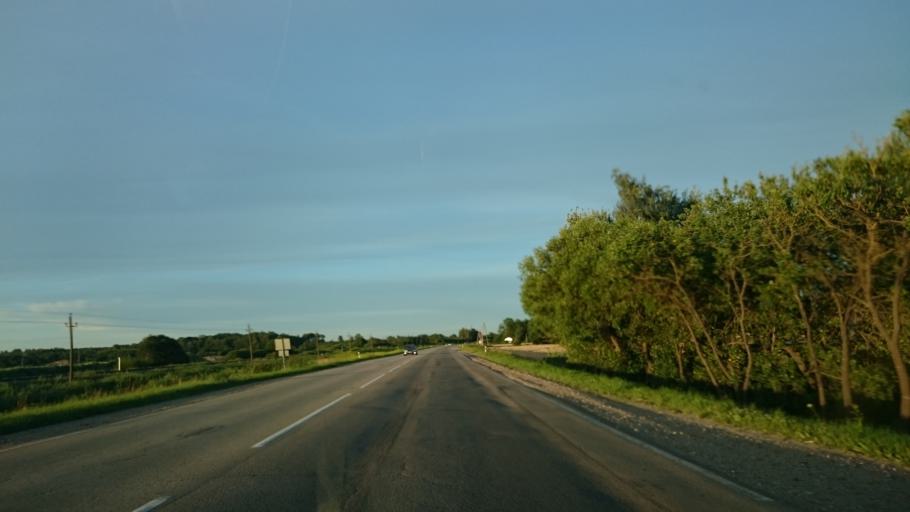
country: LV
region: Broceni
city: Broceni
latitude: 56.6897
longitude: 22.5096
